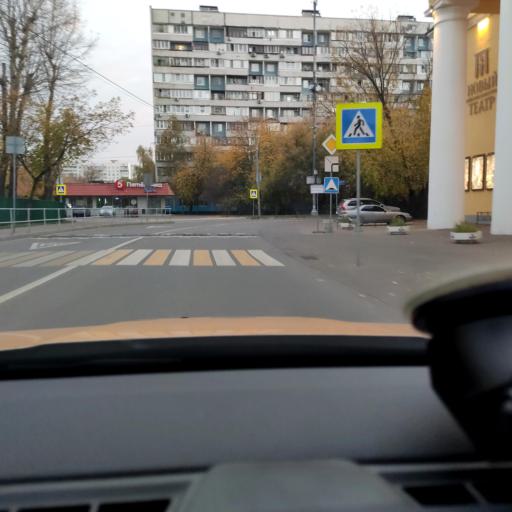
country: RU
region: Moscow
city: Yaroslavskiy
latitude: 55.8740
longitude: 37.7199
